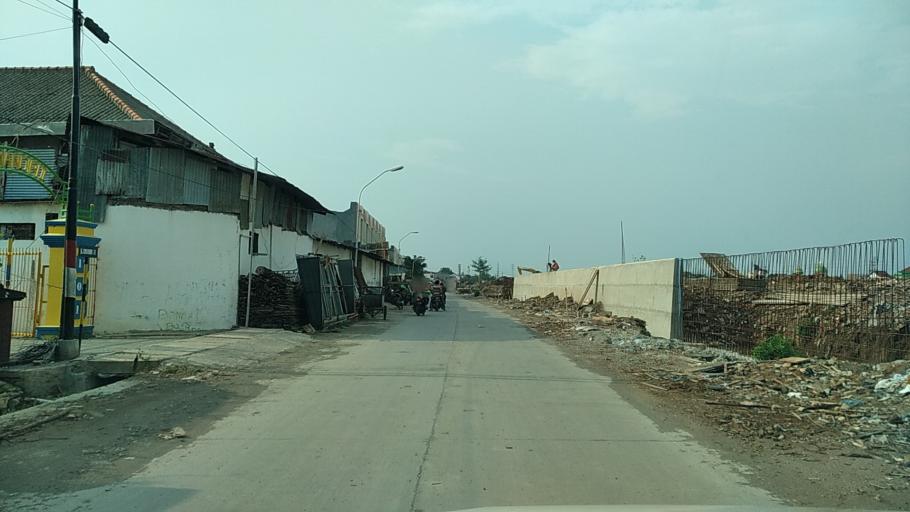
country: ID
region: Central Java
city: Semarang
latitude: -6.9647
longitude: 110.4431
